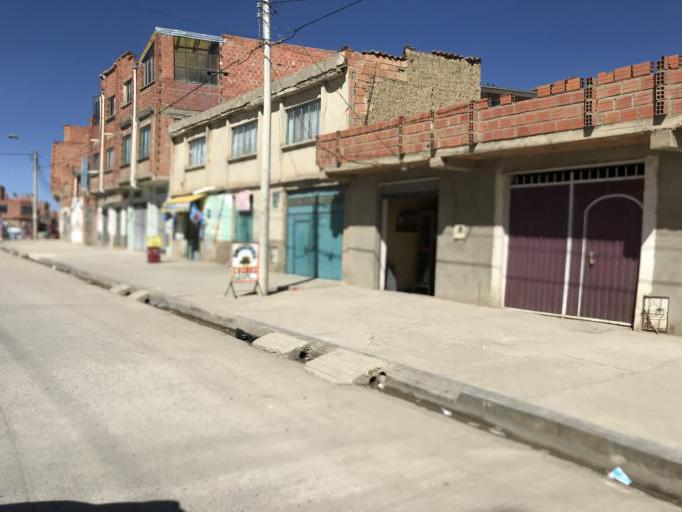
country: BO
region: La Paz
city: La Paz
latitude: -16.4854
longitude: -68.2126
